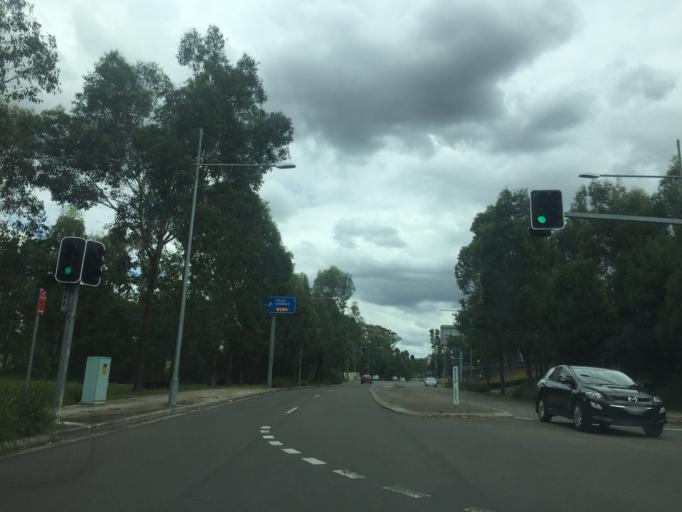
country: AU
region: New South Wales
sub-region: Blacktown
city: Rouse Hill
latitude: -33.6911
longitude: 150.9277
